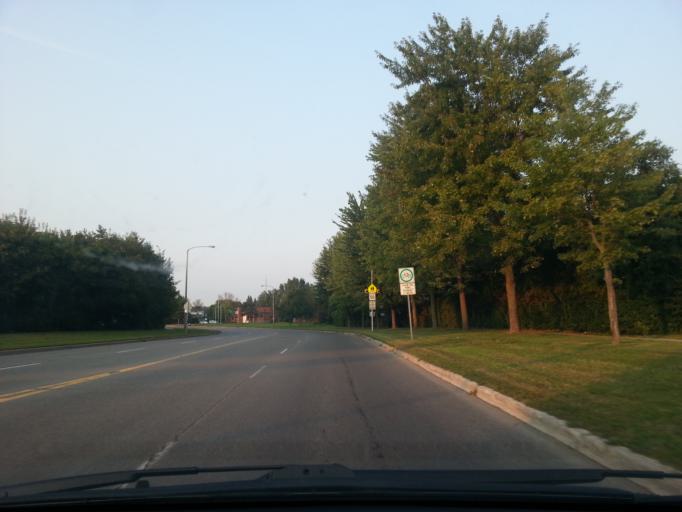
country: CA
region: Quebec
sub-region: Outaouais
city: Gatineau
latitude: 45.4755
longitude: -75.5478
